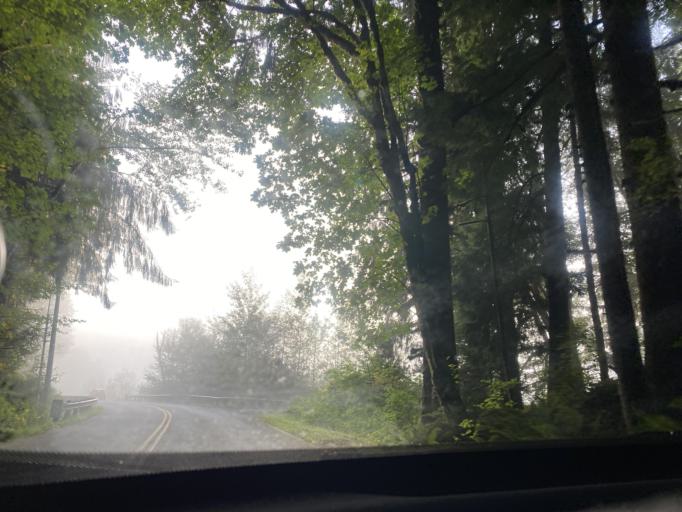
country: US
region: Washington
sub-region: Clallam County
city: Forks
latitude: 47.8100
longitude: -124.0815
